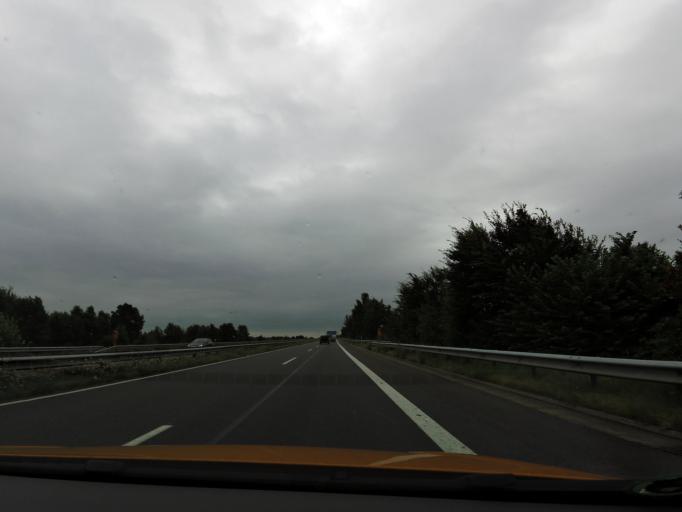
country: DE
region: Lower Saxony
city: Leer
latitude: 53.2823
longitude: 7.4920
